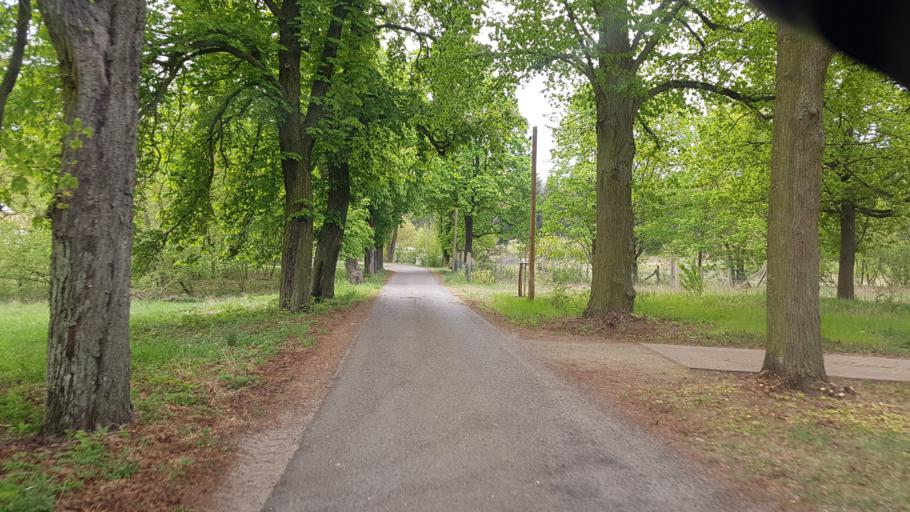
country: DE
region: Brandenburg
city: Altdobern
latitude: 51.6336
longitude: 14.0192
